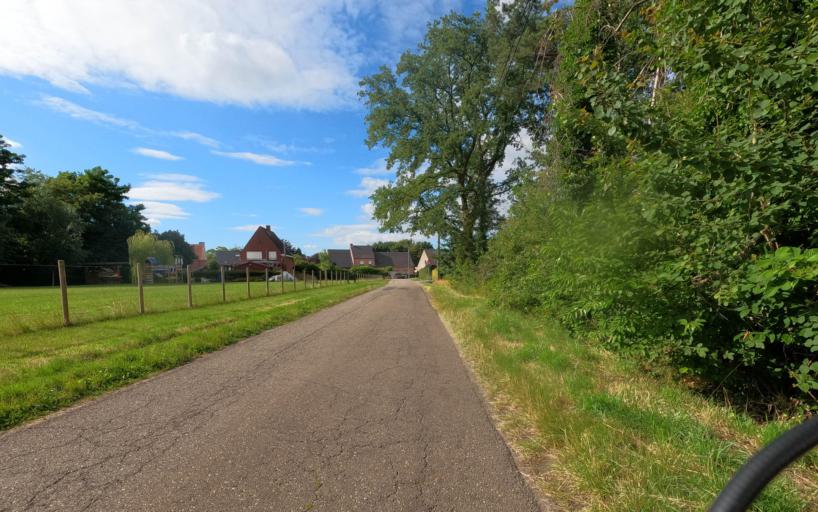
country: BE
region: Flanders
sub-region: Provincie Vlaams-Brabant
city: Tremelo
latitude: 51.0236
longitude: 4.7310
